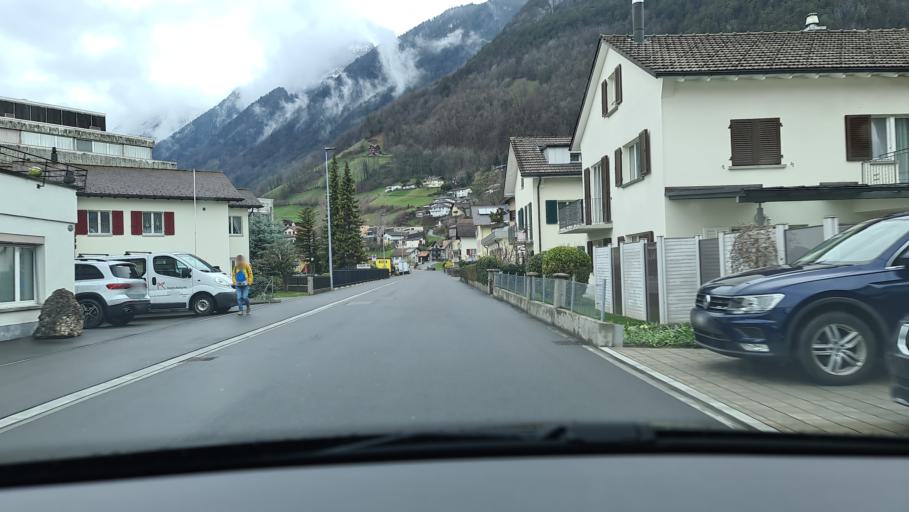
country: CH
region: Schwyz
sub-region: Bezirk Schwyz
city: Ingenbohl
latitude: 47.0019
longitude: 8.6075
